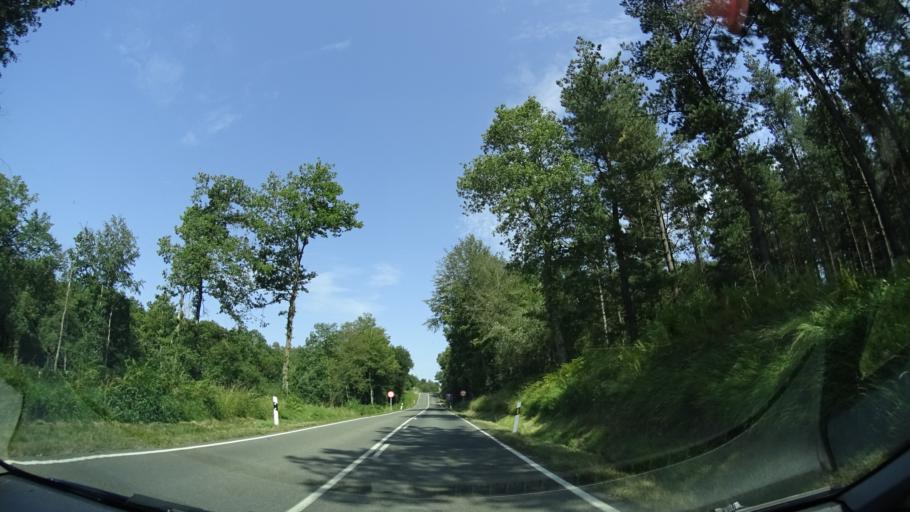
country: ES
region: Basque Country
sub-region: Provincia de Alava
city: Lezama
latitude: 42.9689
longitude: -2.9107
